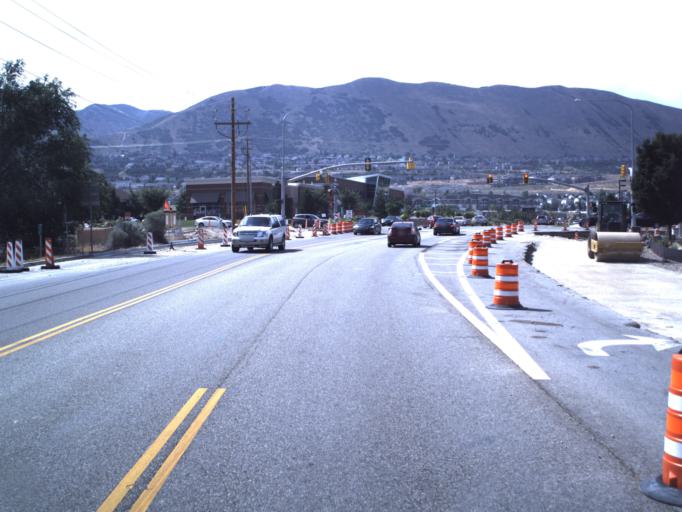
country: US
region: Utah
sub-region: Salt Lake County
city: Draper
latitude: 40.5026
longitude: -111.8855
